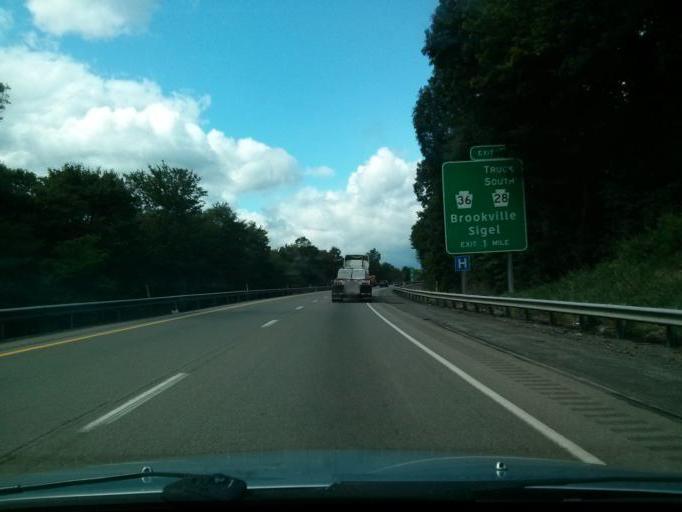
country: US
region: Pennsylvania
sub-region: Jefferson County
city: Brookville
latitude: 41.1702
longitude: -79.0778
